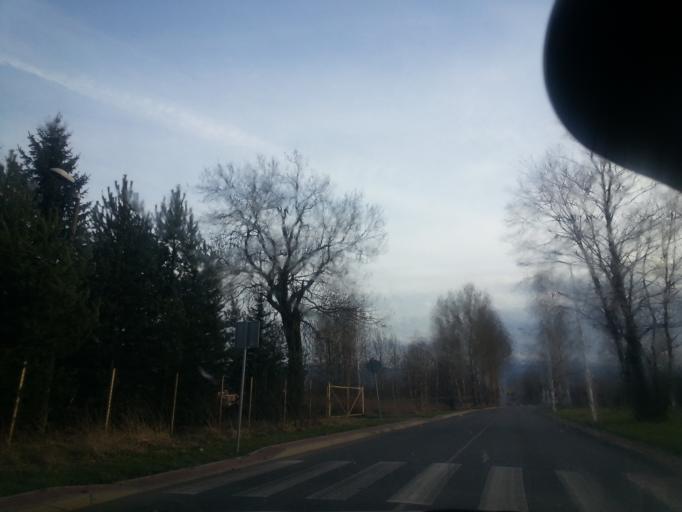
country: PL
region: Lower Silesian Voivodeship
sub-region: Jelenia Gora
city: Jelenia Gora
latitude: 50.8864
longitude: 15.7070
